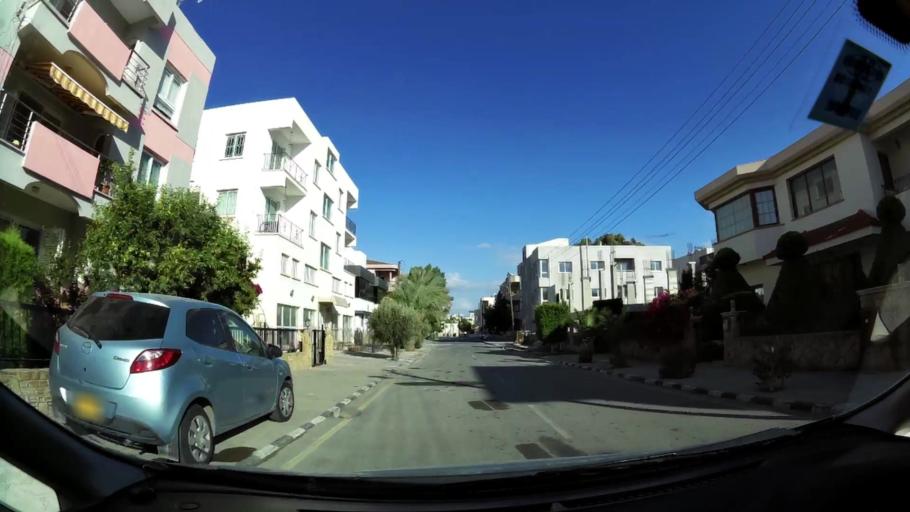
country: CY
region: Lefkosia
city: Nicosia
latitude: 35.1977
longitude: 33.3401
